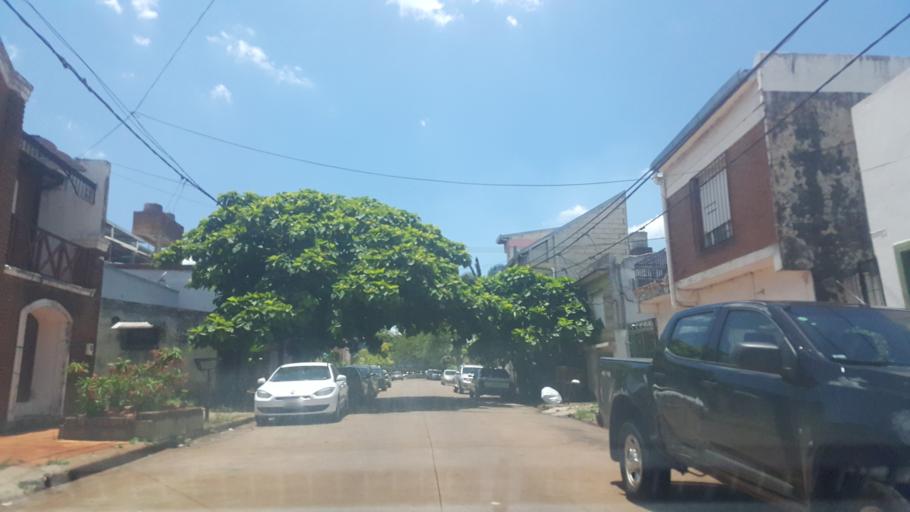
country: AR
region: Misiones
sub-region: Departamento de Capital
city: Posadas
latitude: -27.3710
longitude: -55.9033
